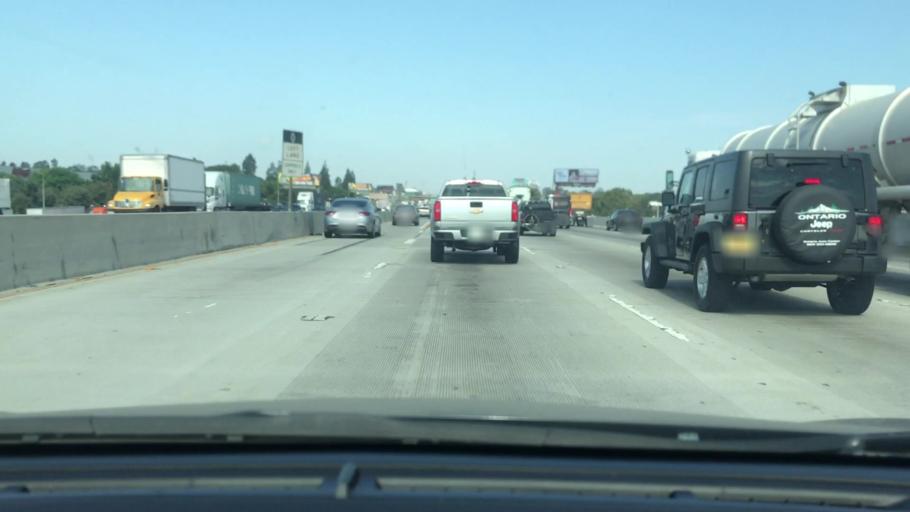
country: US
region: California
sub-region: Los Angeles County
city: Compton
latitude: 33.8742
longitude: -118.2249
